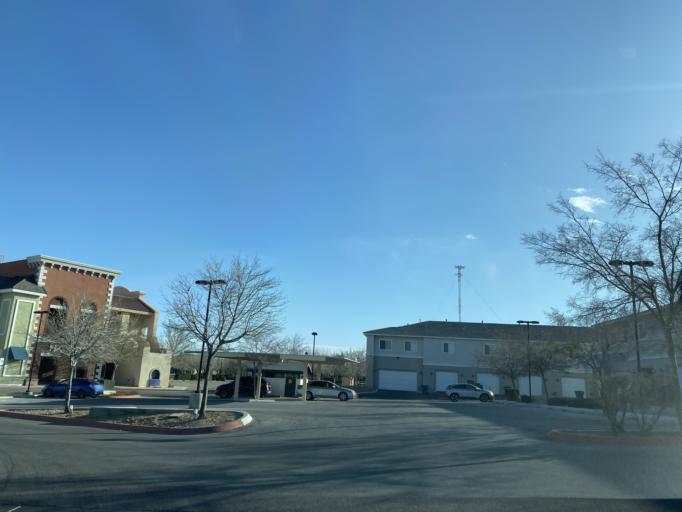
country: US
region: Nevada
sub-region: Clark County
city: Summerlin South
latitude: 36.2987
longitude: -115.2810
